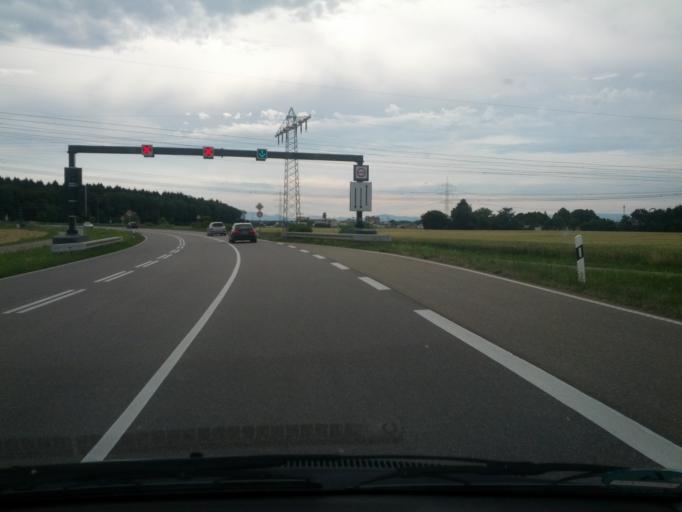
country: DE
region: Baden-Wuerttemberg
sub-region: Freiburg Region
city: Rust
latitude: 48.2592
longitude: 7.7458
